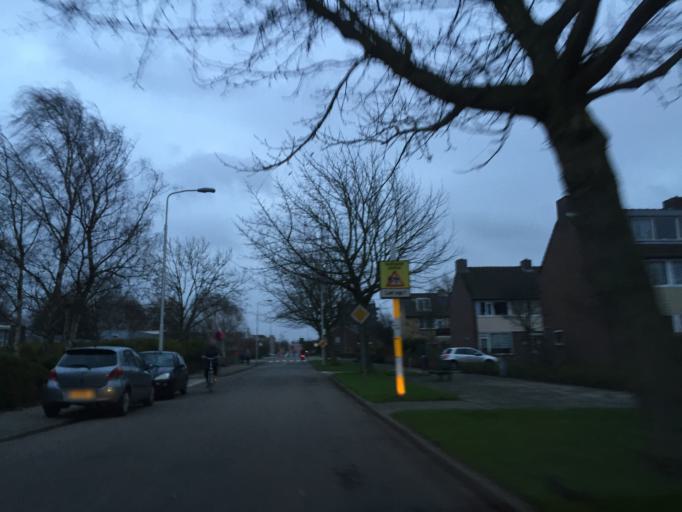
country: NL
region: South Holland
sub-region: Gemeente Pijnacker-Nootdorp
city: Pijnacker
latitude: 52.0221
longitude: 4.4296
